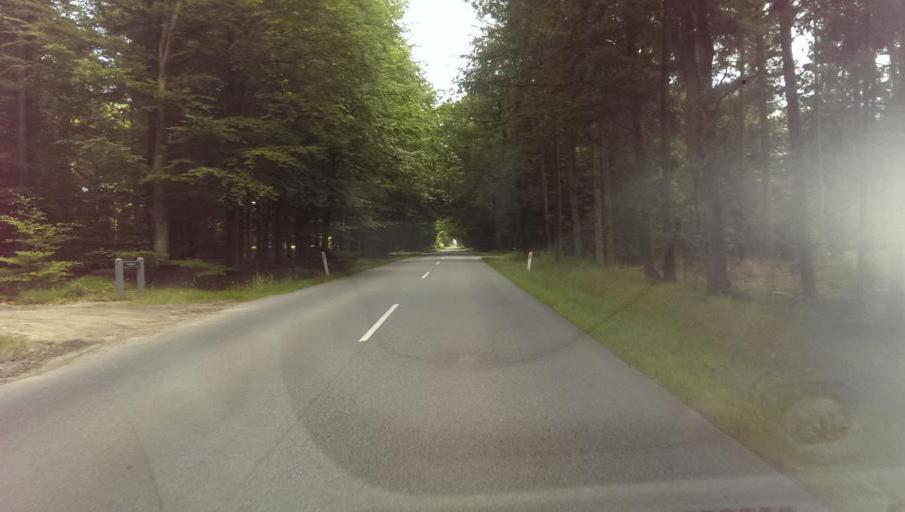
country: DK
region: South Denmark
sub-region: Varde Kommune
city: Varde
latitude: 55.5965
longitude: 8.5278
